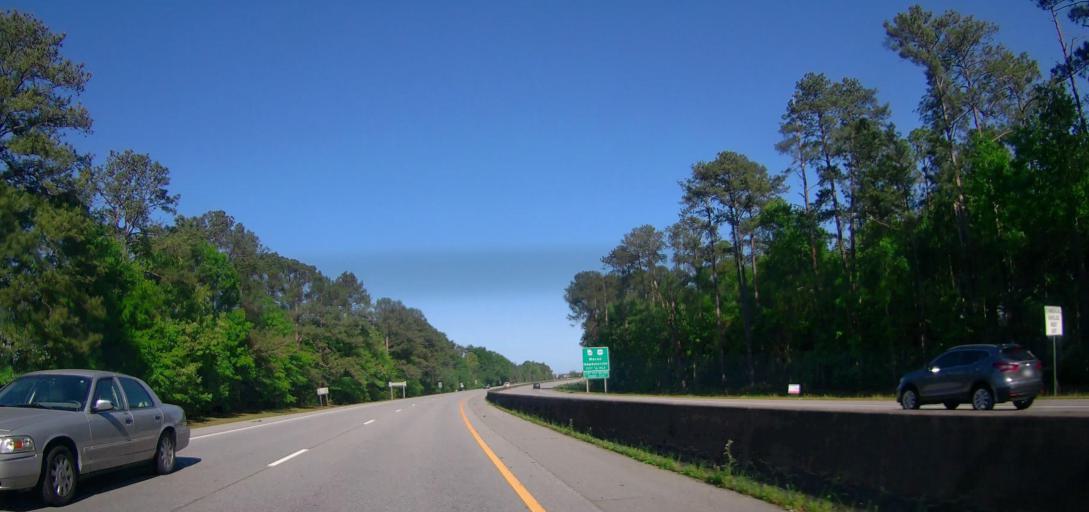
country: US
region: Georgia
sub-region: Houston County
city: Robins Air Force Base
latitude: 32.5944
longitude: -83.5991
